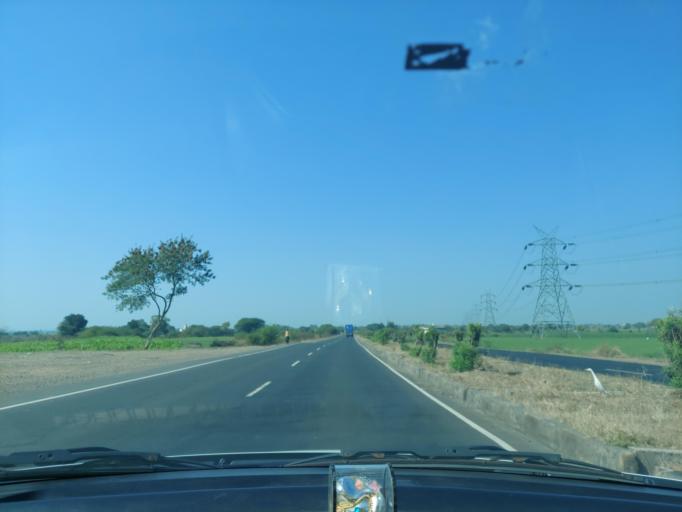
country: IN
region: Madhya Pradesh
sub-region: Indore
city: Manpur
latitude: 22.5051
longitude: 75.5514
